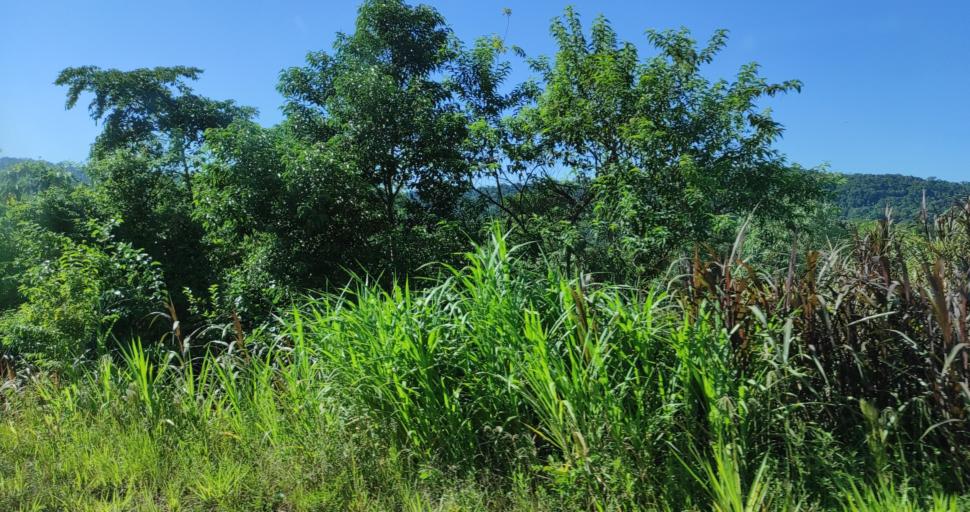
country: AR
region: Misiones
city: El Soberbio
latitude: -27.2478
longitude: -54.0337
